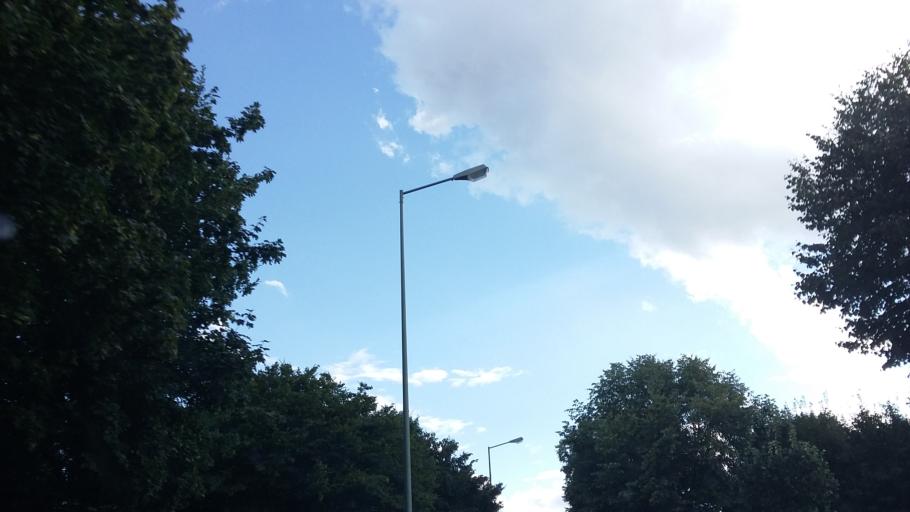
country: DE
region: Bavaria
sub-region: Swabia
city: Augsburg
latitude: 48.3886
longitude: 10.9096
